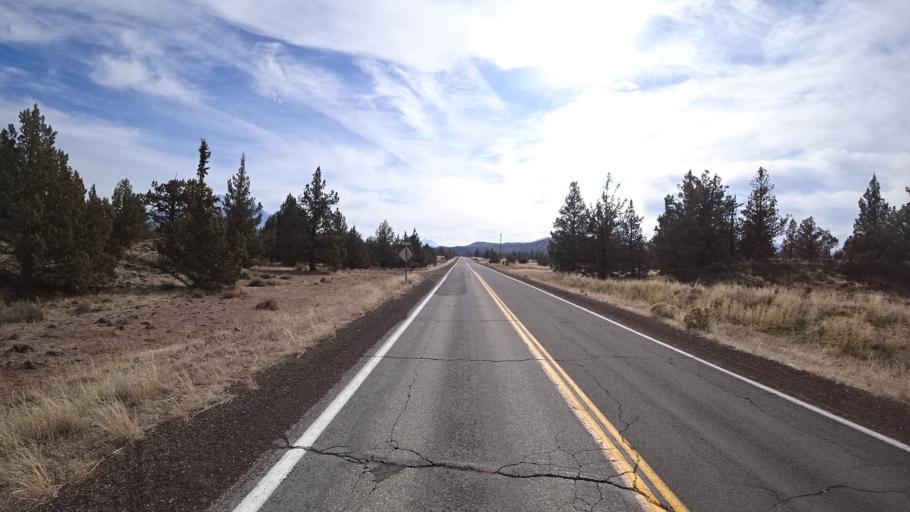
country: US
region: California
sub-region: Siskiyou County
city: Weed
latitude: 41.5894
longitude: -122.4002
